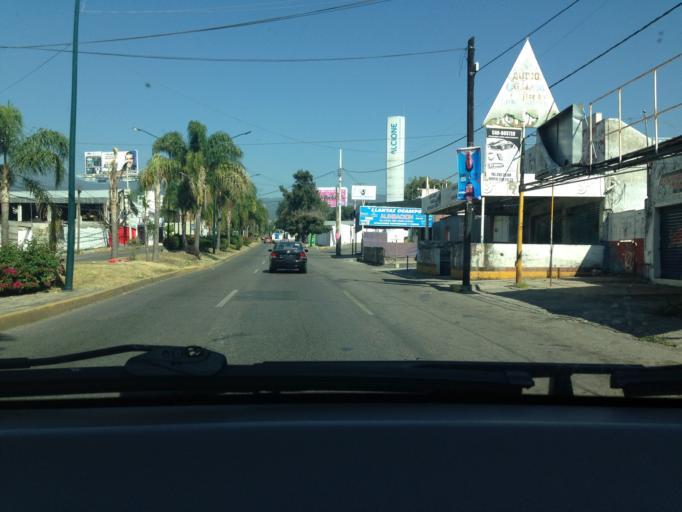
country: MX
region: Morelos
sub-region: Cuernavaca
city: Cuernavaca
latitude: 18.9477
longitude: -99.2343
